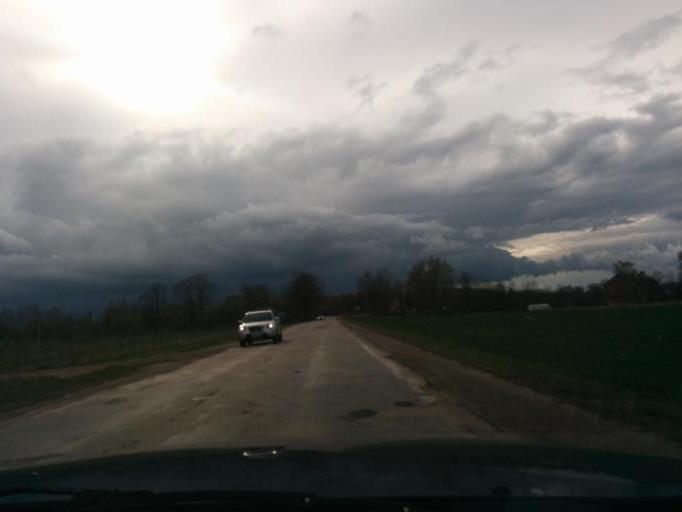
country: LT
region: Siauliu apskritis
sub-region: Joniskis
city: Joniskis
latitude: 56.4183
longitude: 23.5701
